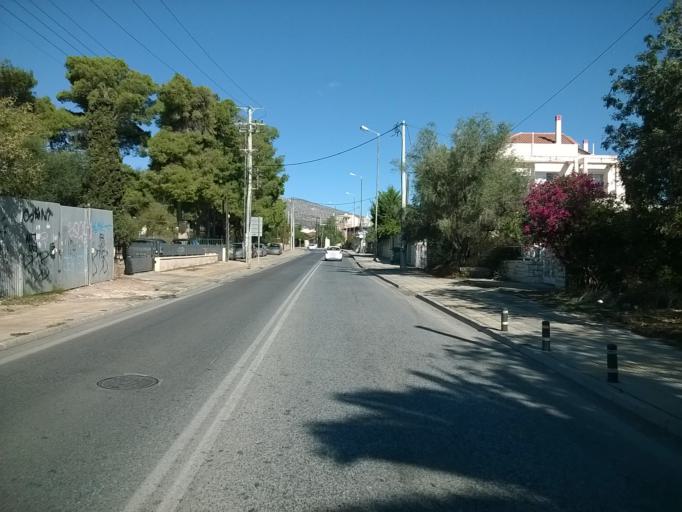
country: GR
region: Attica
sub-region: Nomarchia Anatolikis Attikis
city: Vari
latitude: 37.8230
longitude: 23.8040
